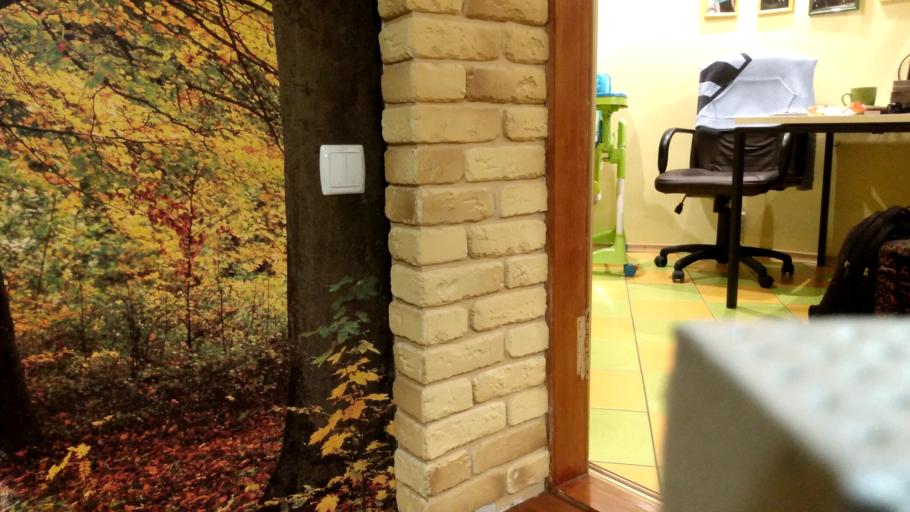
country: RU
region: Republic of Karelia
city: Pudozh
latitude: 61.6273
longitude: 37.7342
